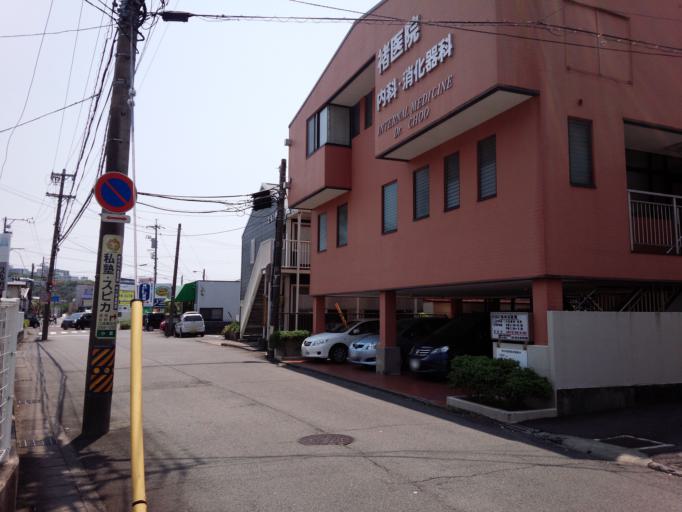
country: JP
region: Shizuoka
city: Shizuoka-shi
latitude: 34.9739
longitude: 138.4245
